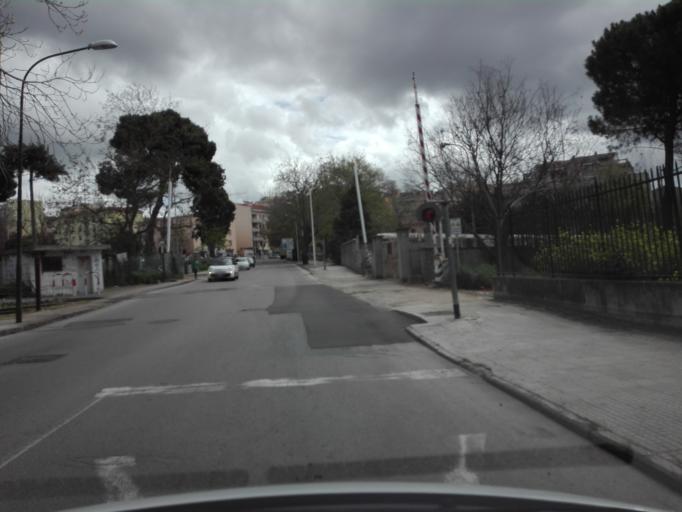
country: IT
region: Sardinia
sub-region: Provincia di Sassari
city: Sassari
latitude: 40.7382
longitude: 8.5594
